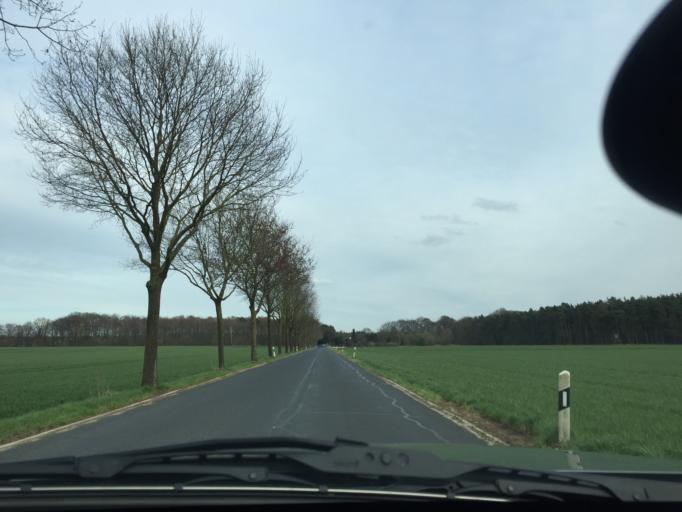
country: DE
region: North Rhine-Westphalia
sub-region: Regierungsbezirk Dusseldorf
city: Kleve
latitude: 51.7403
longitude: 6.1518
